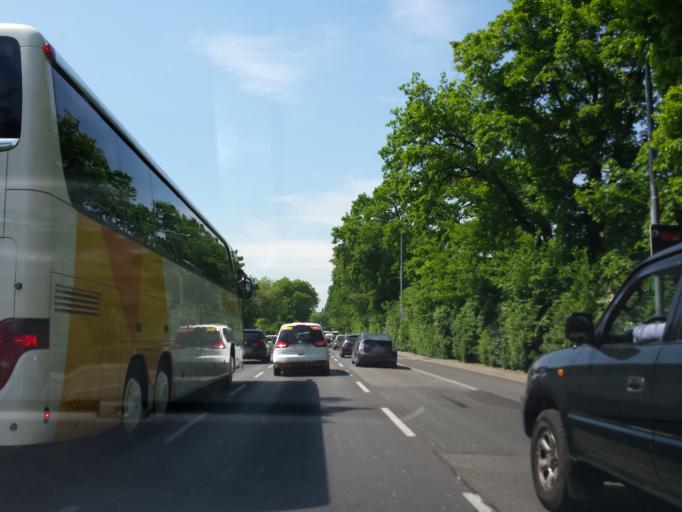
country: AT
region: Vienna
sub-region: Wien Stadt
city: Vienna
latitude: 48.1868
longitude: 16.3179
